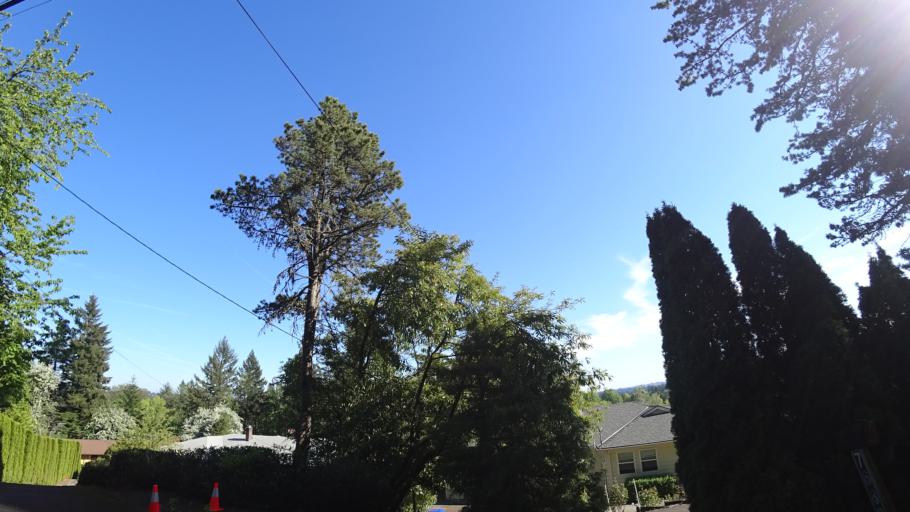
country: US
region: Oregon
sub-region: Washington County
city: West Slope
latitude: 45.4969
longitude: -122.7557
